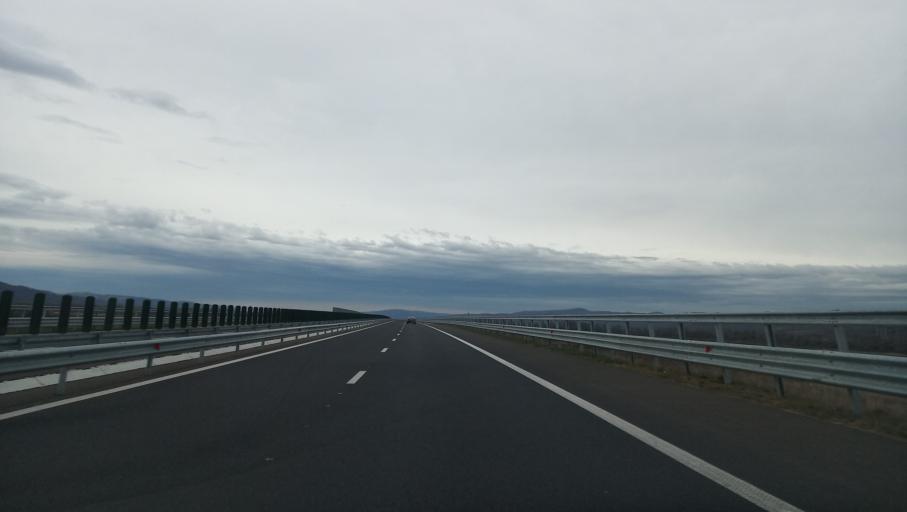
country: RO
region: Hunedoara
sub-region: Comuna Ilia
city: Ilia
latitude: 45.9475
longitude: 22.7094
